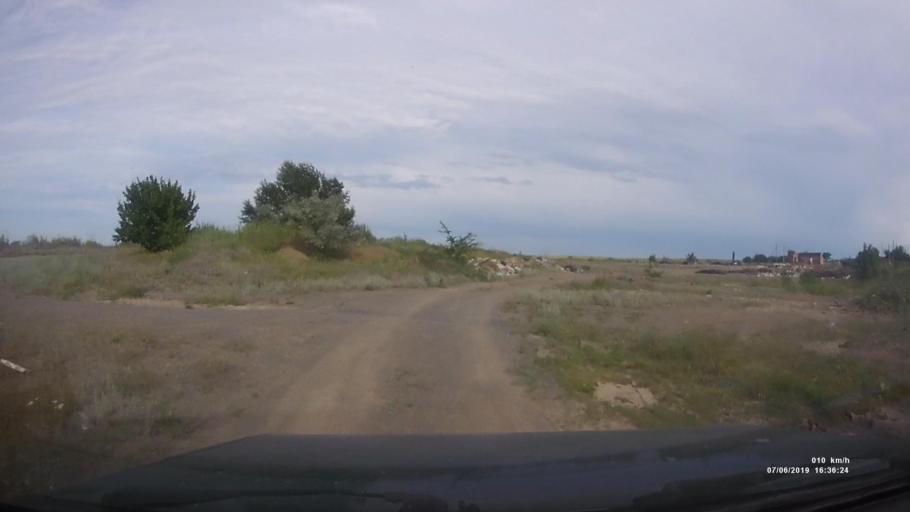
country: RU
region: Rostov
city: Staraya Stanitsa
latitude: 48.2534
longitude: 40.3519
